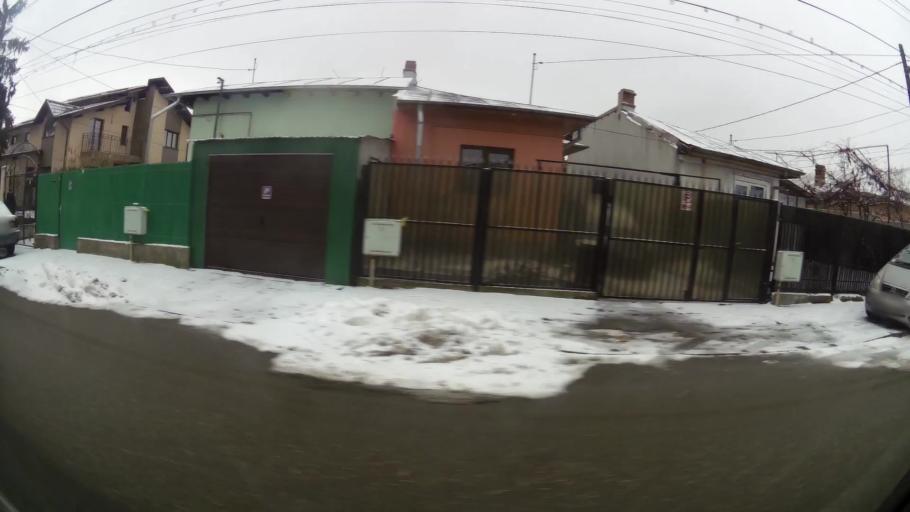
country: RO
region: Prahova
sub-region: Comuna Barcanesti
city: Tatarani
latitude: 44.9321
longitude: 26.0505
